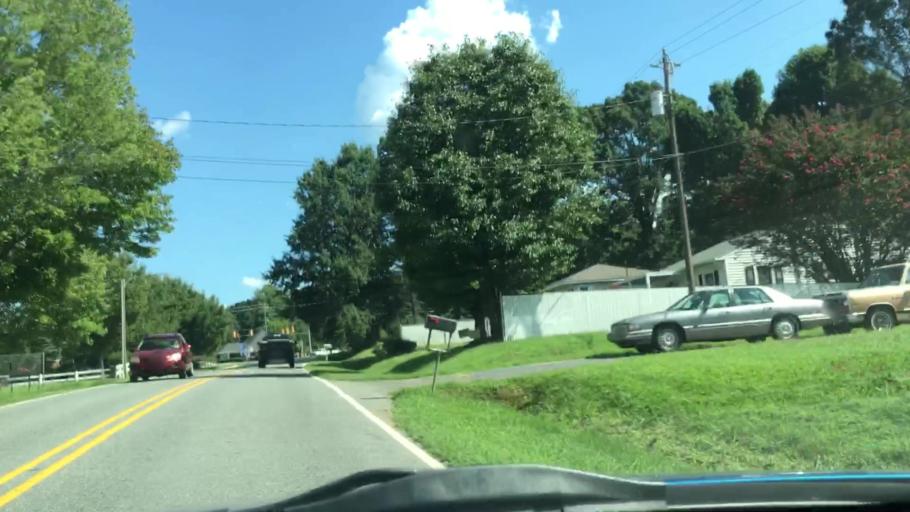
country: US
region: North Carolina
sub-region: Randolph County
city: Asheboro
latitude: 35.7463
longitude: -79.8090
